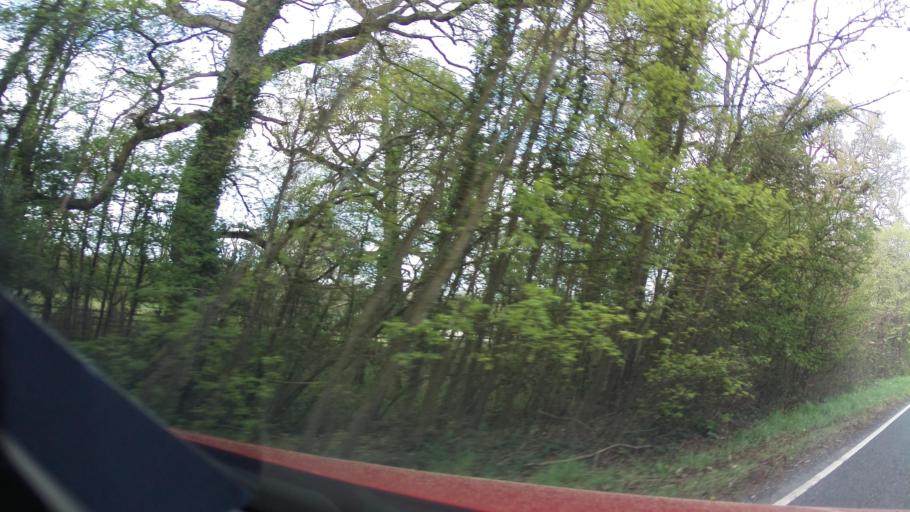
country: GB
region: England
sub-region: Hampshire
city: Chandlers Ford
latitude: 51.0156
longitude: -1.3964
